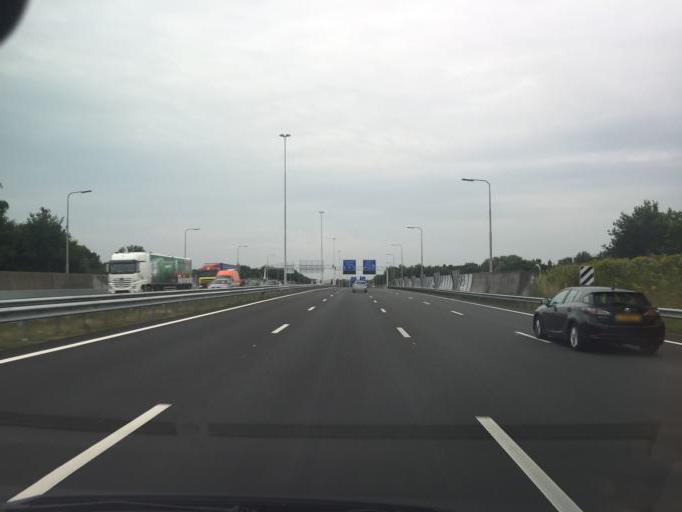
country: NL
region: North Brabant
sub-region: Gemeente Best
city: Best
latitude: 51.5024
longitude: 5.4181
